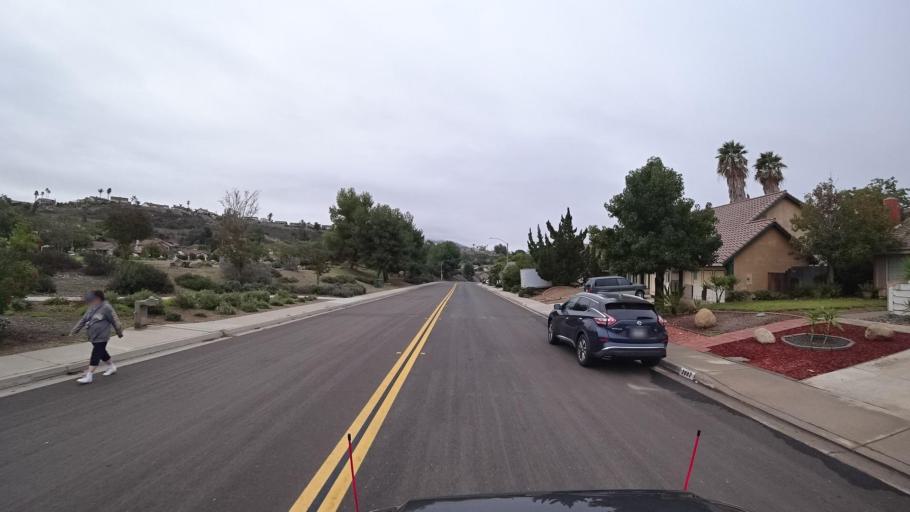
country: US
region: California
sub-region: San Diego County
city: Rancho San Diego
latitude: 32.7582
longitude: -116.9122
